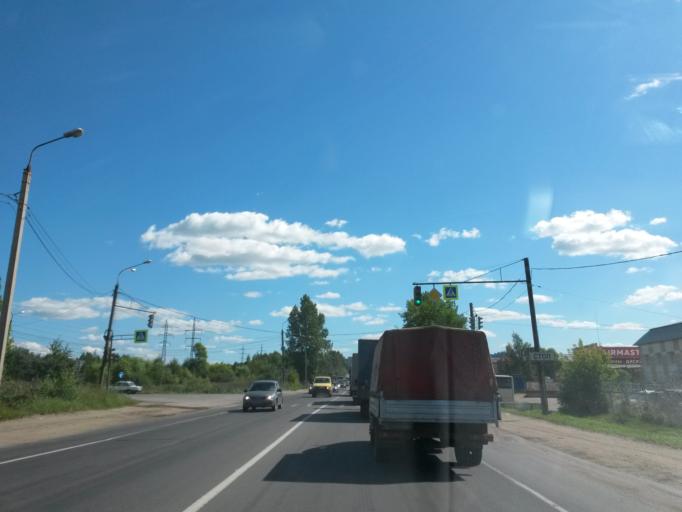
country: RU
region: Jaroslavl
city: Yaroslavl
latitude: 57.5949
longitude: 39.8120
